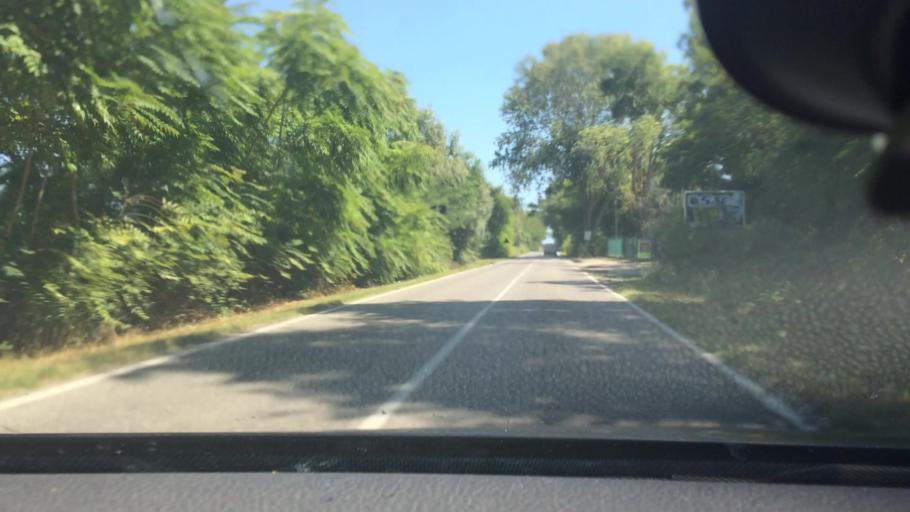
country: IT
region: Emilia-Romagna
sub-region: Provincia di Ferrara
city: Porto Garibaldi
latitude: 44.6887
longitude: 12.2305
